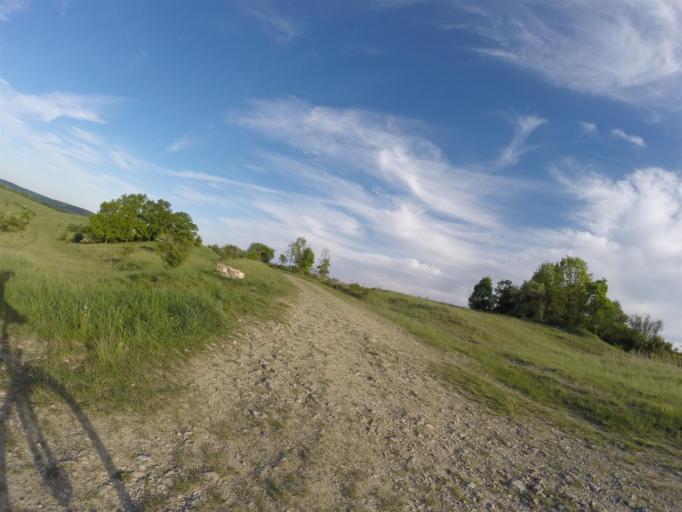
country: DE
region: Thuringia
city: Jena
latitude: 50.9507
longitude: 11.5714
